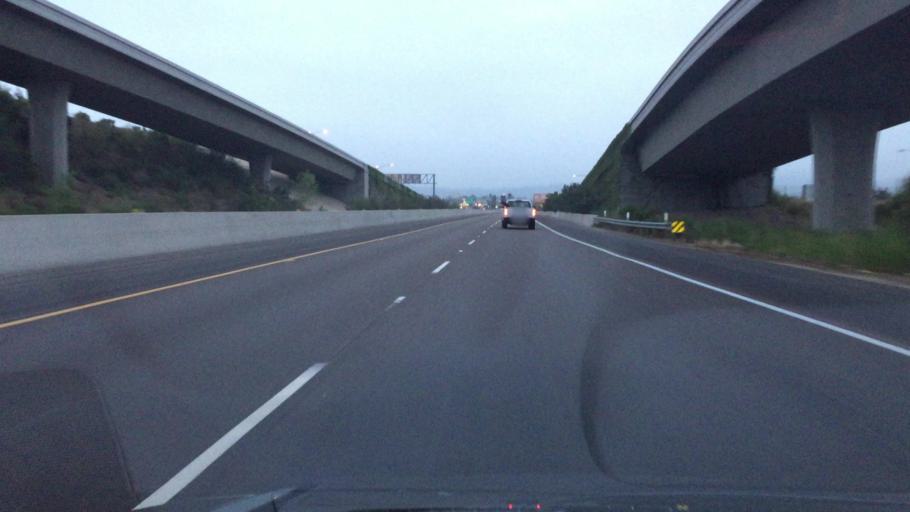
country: US
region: California
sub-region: San Diego County
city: Santee
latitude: 32.8303
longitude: -116.9620
